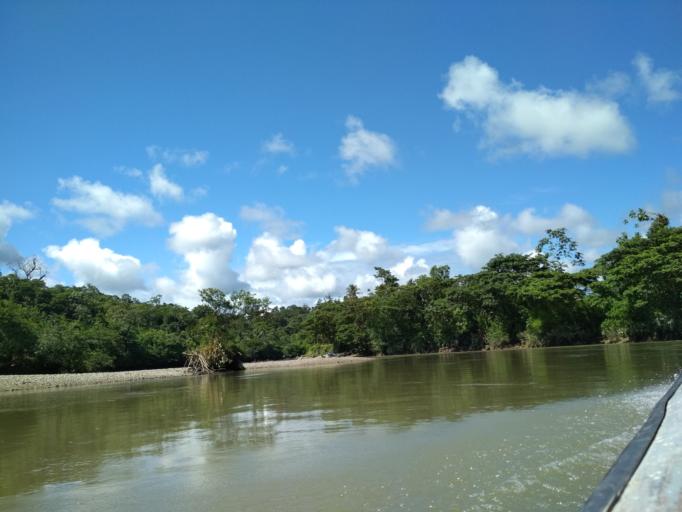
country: CO
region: Cauca
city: Timbiqui
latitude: 2.7605
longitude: -77.6635
